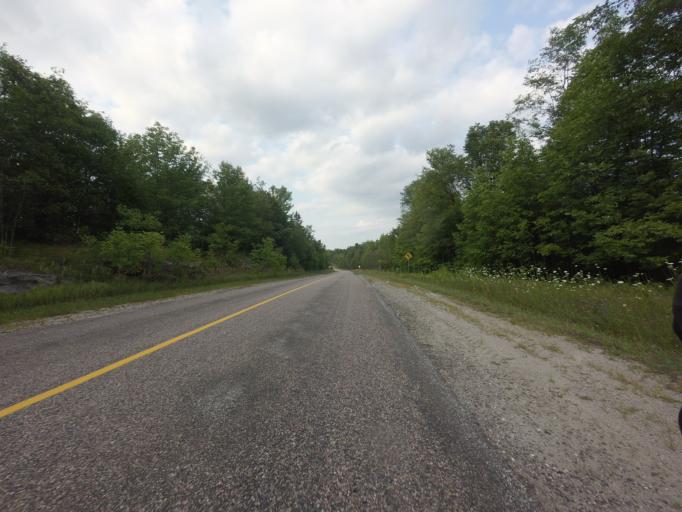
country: CA
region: Ontario
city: Perth
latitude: 44.8835
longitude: -76.6957
